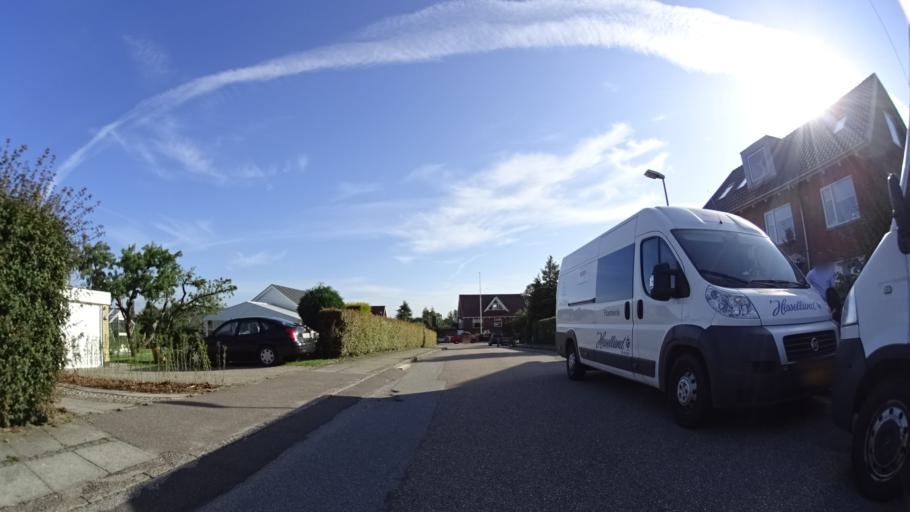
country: DK
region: Central Jutland
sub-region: Arhus Kommune
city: Stavtrup
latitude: 56.1170
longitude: 10.1623
